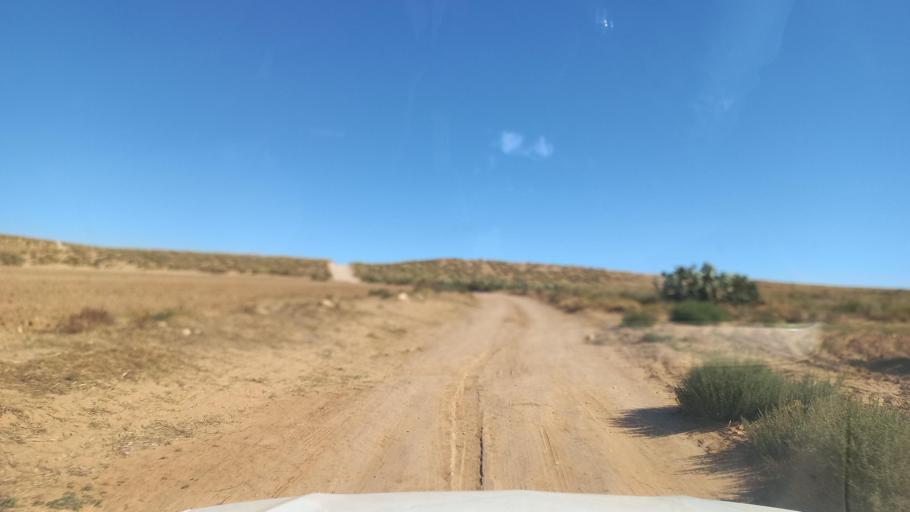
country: TN
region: Al Qasrayn
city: Sbiba
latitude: 35.4046
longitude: 9.0917
